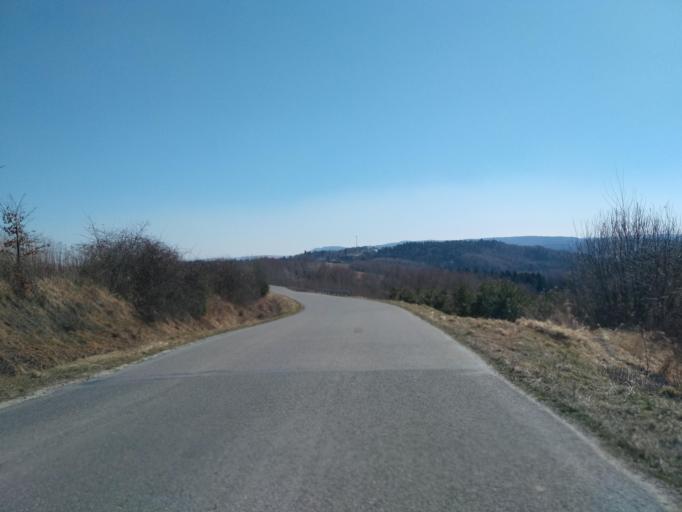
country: PL
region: Subcarpathian Voivodeship
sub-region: Powiat ropczycko-sedziszowski
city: Niedzwiada
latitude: 49.9628
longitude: 21.4755
